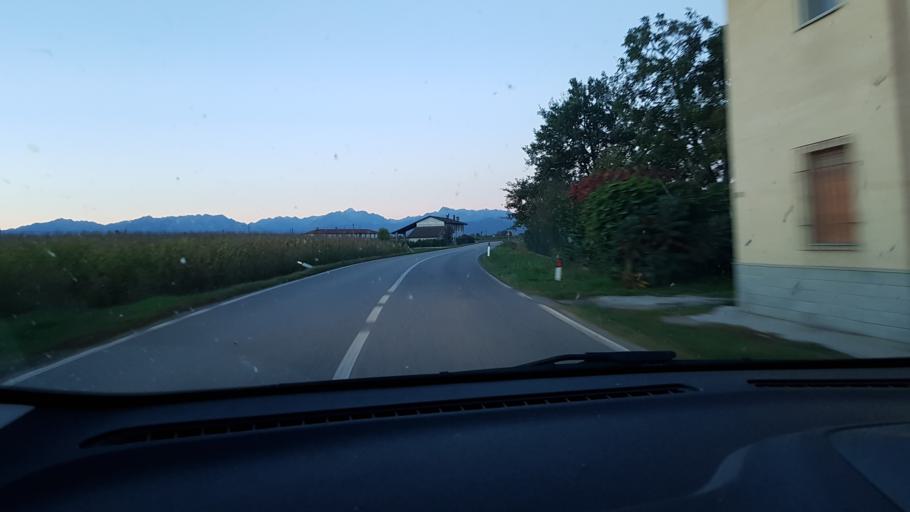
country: IT
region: Piedmont
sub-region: Provincia di Cuneo
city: Vottignasco
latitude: 44.5586
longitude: 7.5654
